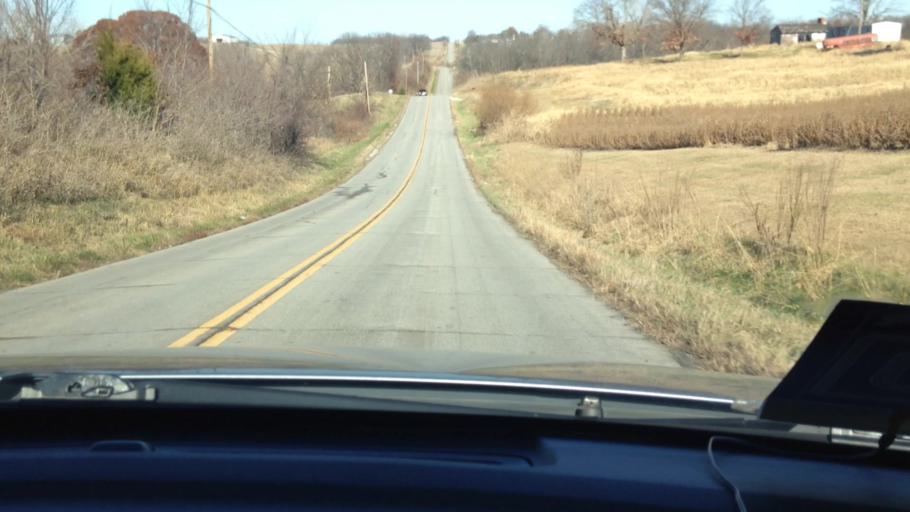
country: US
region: Missouri
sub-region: Platte County
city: Weston
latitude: 39.4343
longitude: -94.9007
